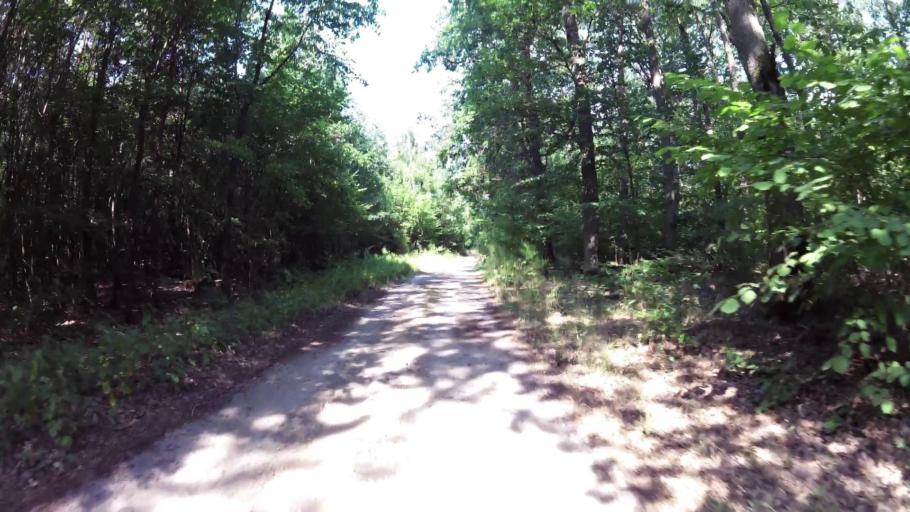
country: PL
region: West Pomeranian Voivodeship
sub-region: Powiat gryfinski
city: Moryn
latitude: 52.8796
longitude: 14.4298
